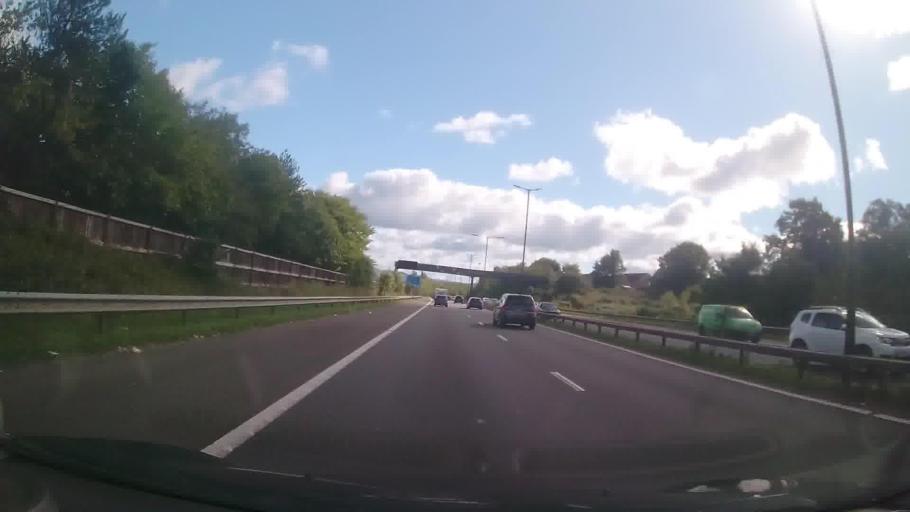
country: GB
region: Wales
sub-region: City and County of Swansea
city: Clydach
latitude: 51.6582
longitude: -3.8629
